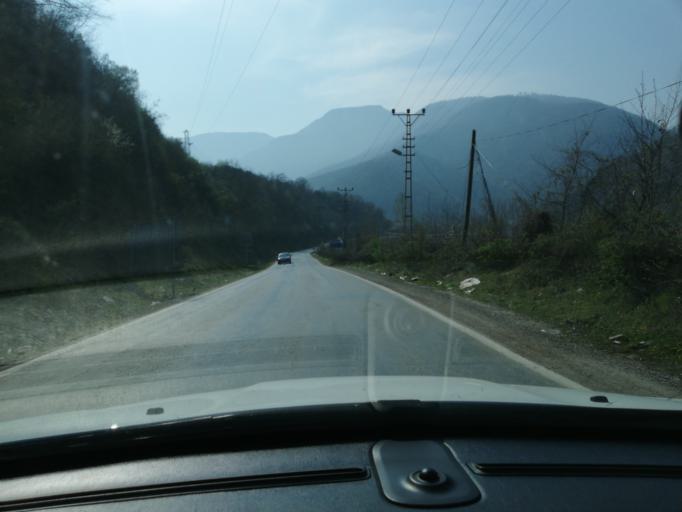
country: TR
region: Karabuk
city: Yenice
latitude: 41.2106
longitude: 32.3659
